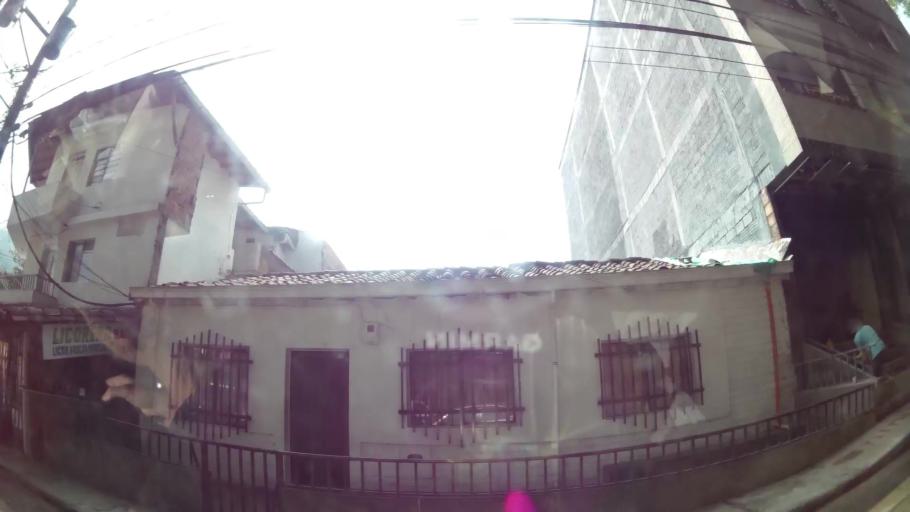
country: CO
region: Antioquia
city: La Estrella
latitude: 6.1723
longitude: -75.6275
